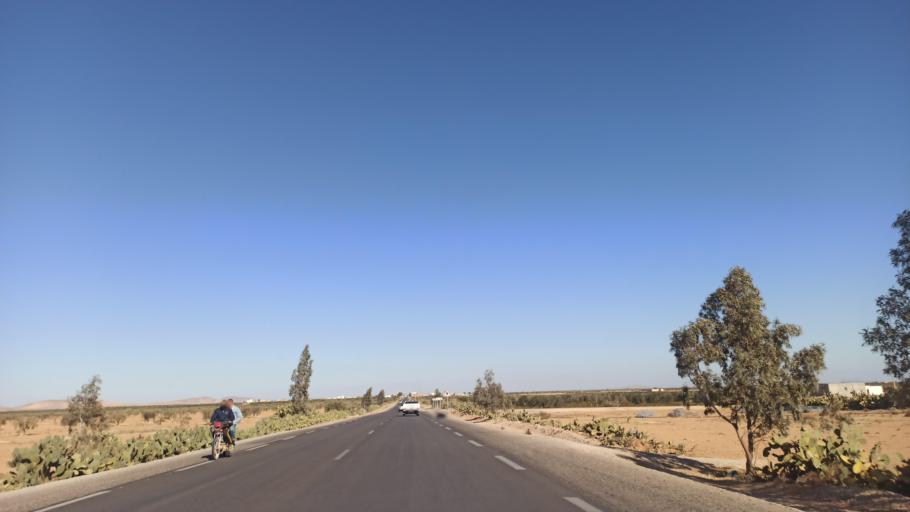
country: TN
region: Sidi Bu Zayd
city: Bi'r al Hufayy
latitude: 34.9591
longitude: 9.2194
